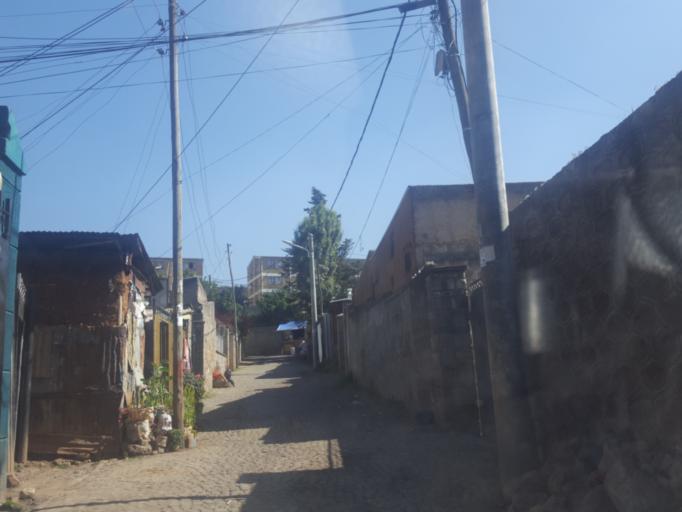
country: ET
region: Adis Abeba
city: Addis Ababa
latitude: 9.0547
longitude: 38.7211
